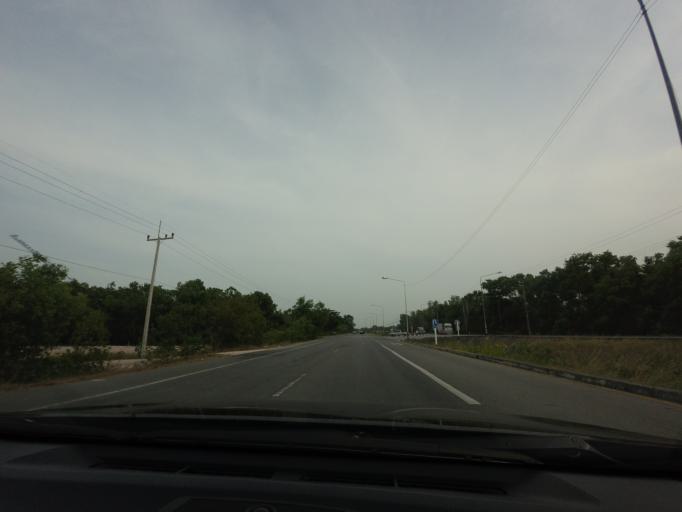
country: TH
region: Songkhla
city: Thepha
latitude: 6.9103
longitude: 100.9030
